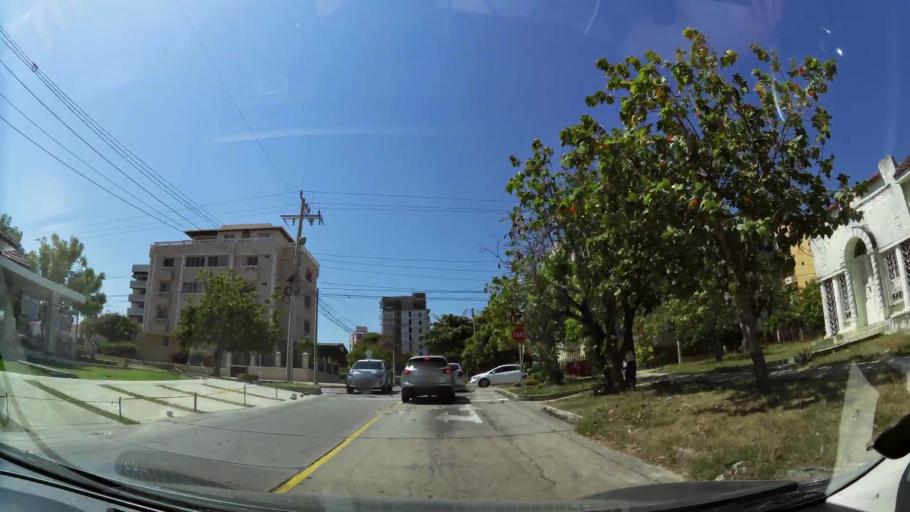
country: CO
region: Atlantico
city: Barranquilla
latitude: 10.9992
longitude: -74.7954
